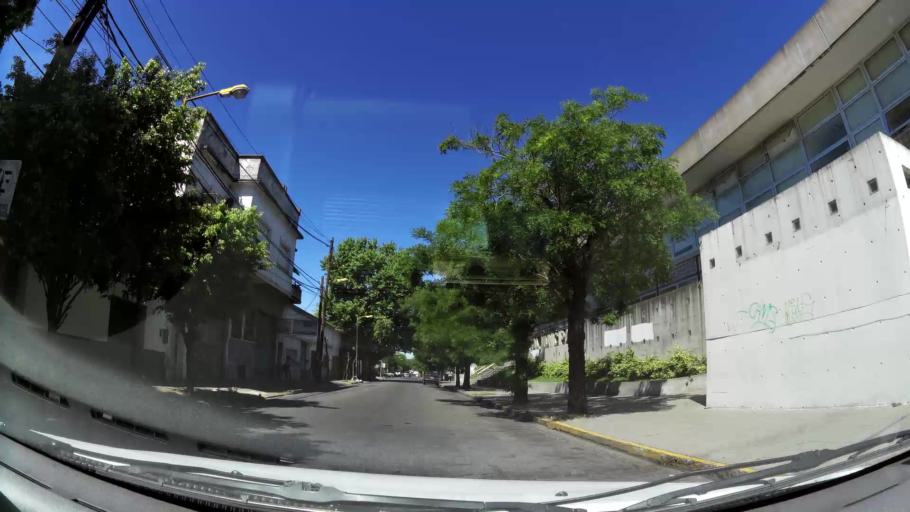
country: AR
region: Buenos Aires
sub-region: Partido de General San Martin
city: General San Martin
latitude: -34.5811
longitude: -58.5435
